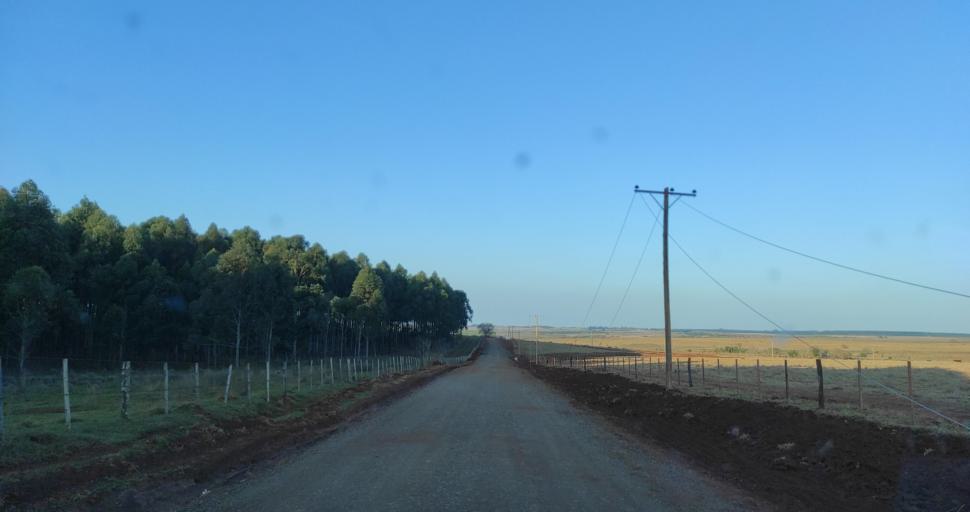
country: PY
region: Itapua
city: San Juan del Parana
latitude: -27.4230
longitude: -56.0845
